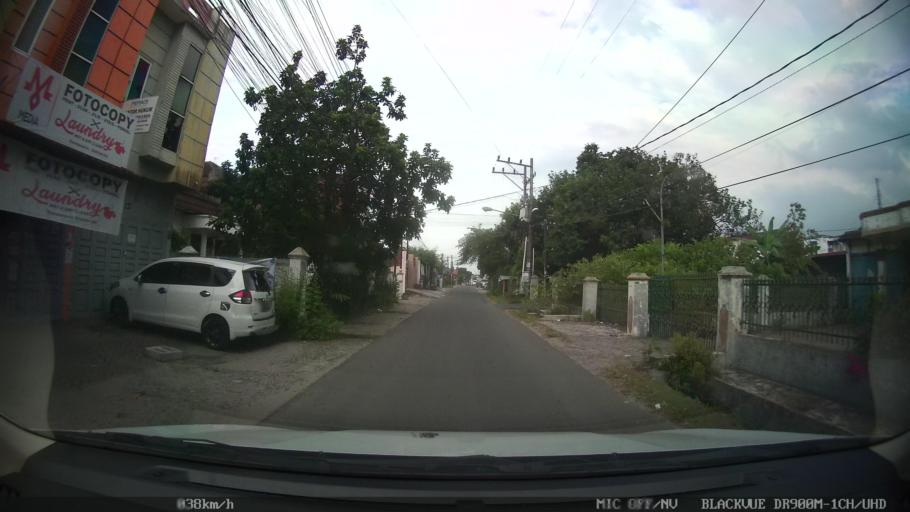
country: ID
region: North Sumatra
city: Sunggal
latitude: 3.5549
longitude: 98.6284
